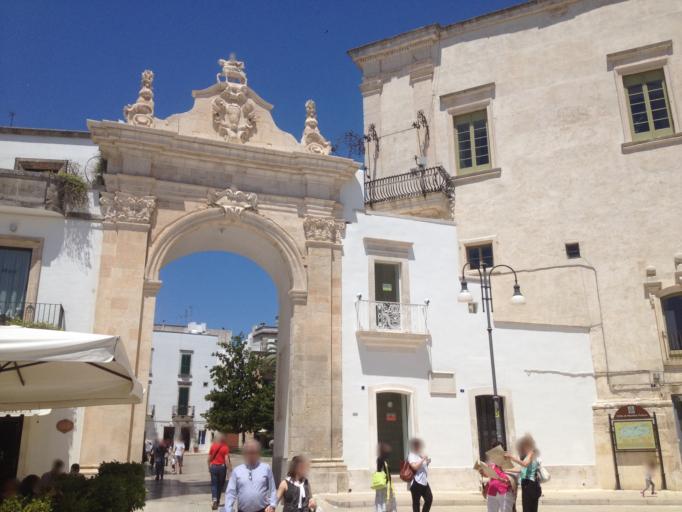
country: IT
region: Apulia
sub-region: Provincia di Taranto
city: Martina Franca
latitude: 40.7047
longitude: 17.3394
